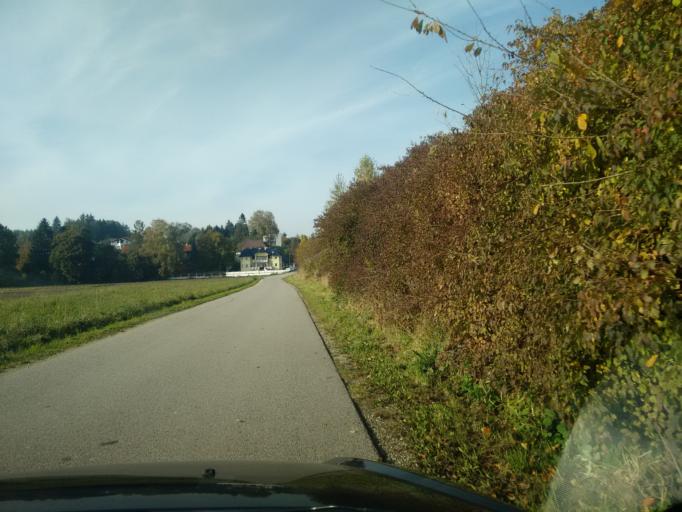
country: AT
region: Upper Austria
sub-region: Wels Stadt
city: Wels
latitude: 48.1854
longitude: 14.0017
